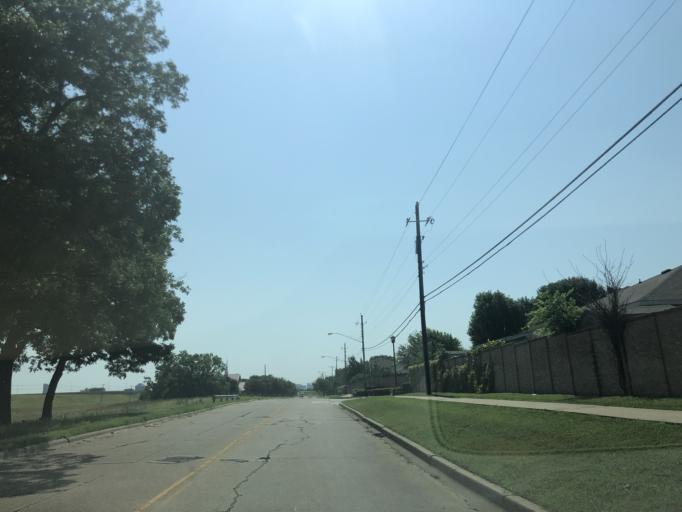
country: US
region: Texas
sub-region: Dallas County
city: Dallas
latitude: 32.7926
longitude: -96.8627
